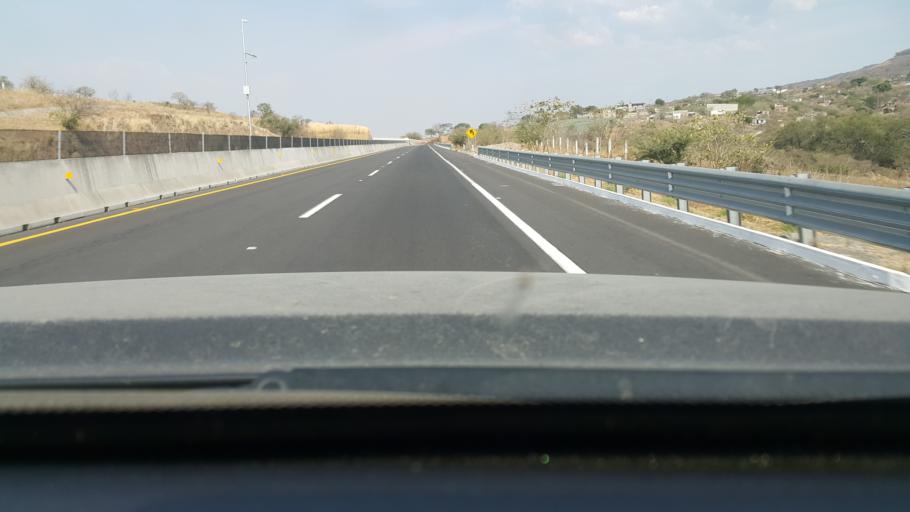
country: MX
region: Nayarit
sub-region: Ahuacatlan
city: Ahuacatlan
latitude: 21.0561
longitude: -104.5246
